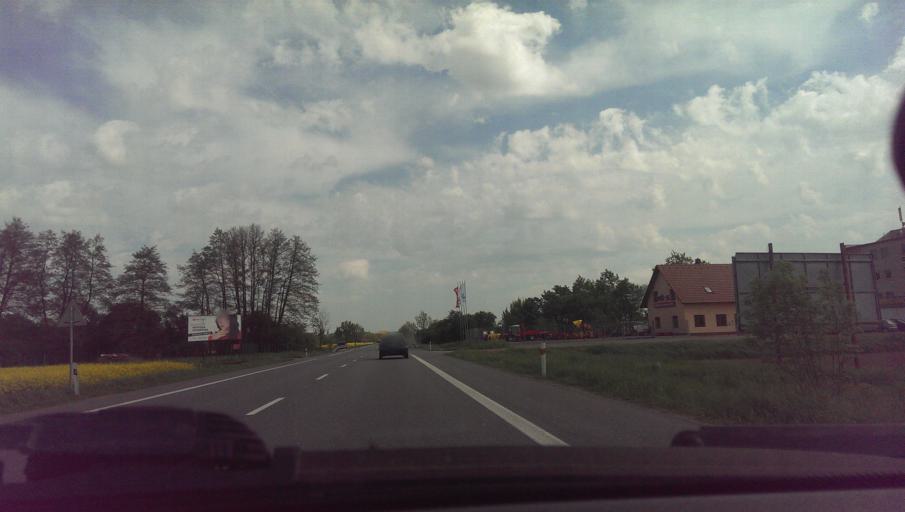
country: CZ
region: Zlin
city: Babice
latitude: 49.1285
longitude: 17.4816
